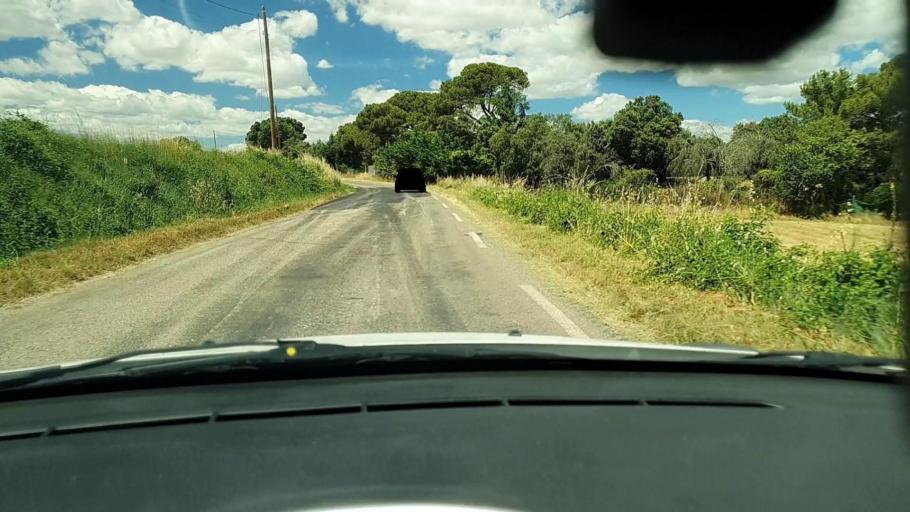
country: FR
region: Languedoc-Roussillon
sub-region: Departement du Gard
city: Poulx
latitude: 43.9553
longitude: 4.4410
